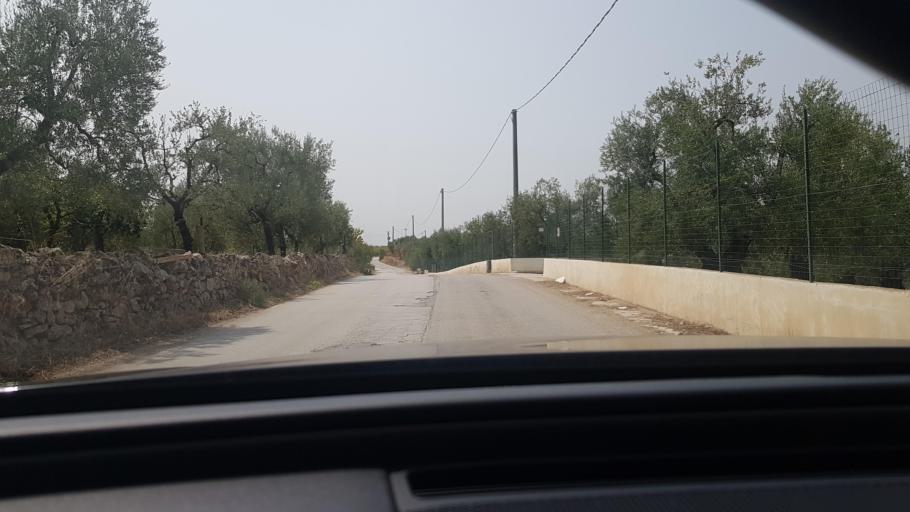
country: IT
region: Apulia
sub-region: Provincia di Barletta - Andria - Trani
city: Andria
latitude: 41.2235
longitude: 16.2661
